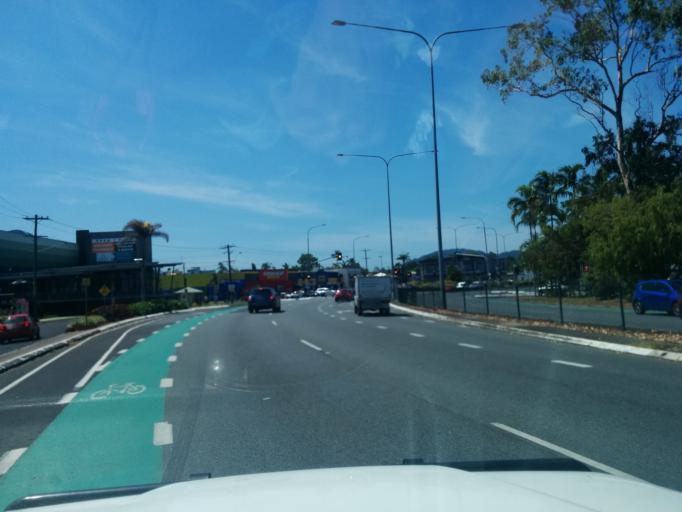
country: AU
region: Queensland
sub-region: Cairns
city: Woree
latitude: -16.9461
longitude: 145.7384
